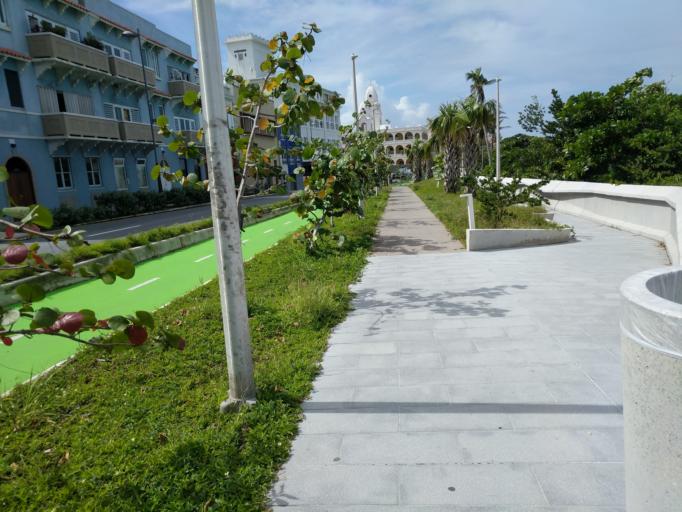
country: PR
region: San Juan
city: San Juan
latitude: 18.4657
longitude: -66.0968
